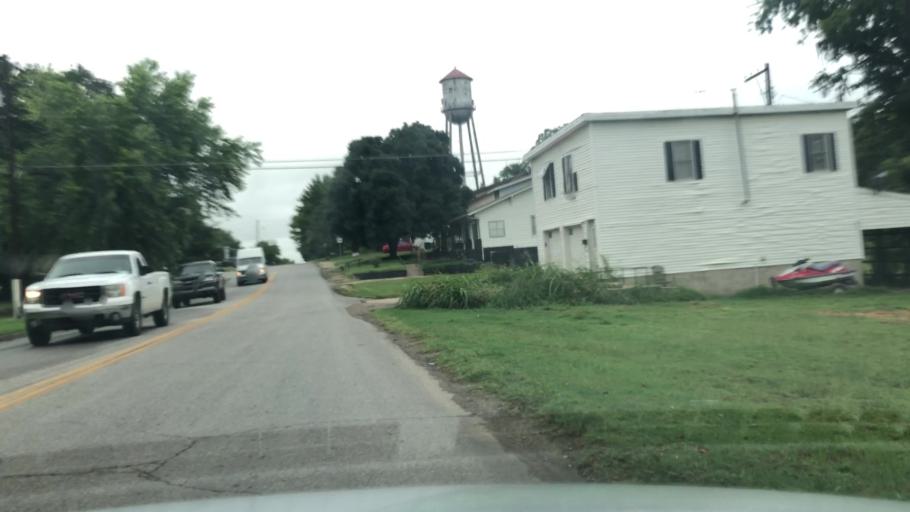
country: US
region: Oklahoma
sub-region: Nowata County
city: Nowata
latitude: 36.7017
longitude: -95.6406
